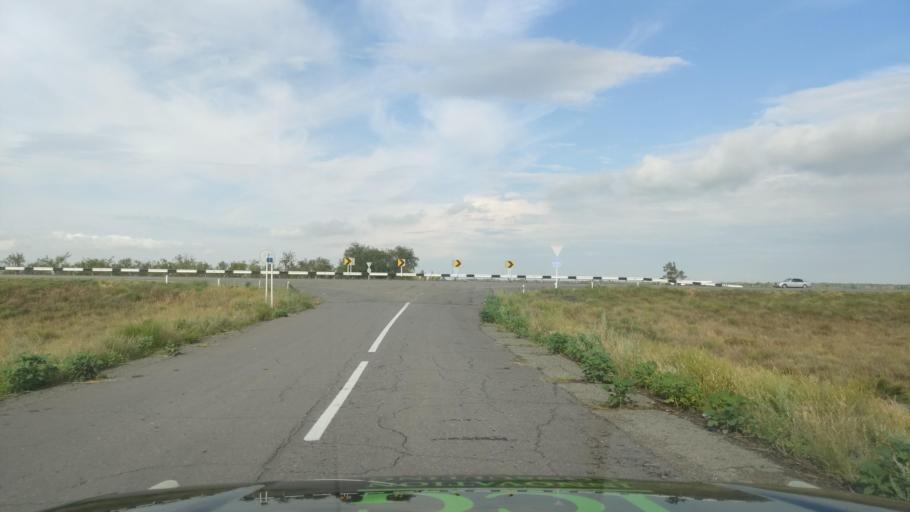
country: KZ
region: Pavlodar
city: Leninskiy
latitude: 52.4782
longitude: 76.8389
